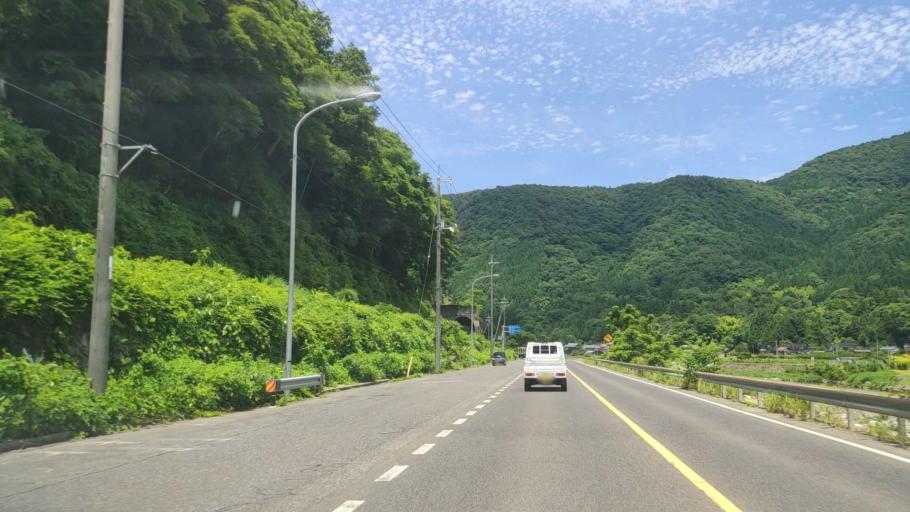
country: JP
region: Tottori
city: Tottori
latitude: 35.3643
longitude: 134.3780
